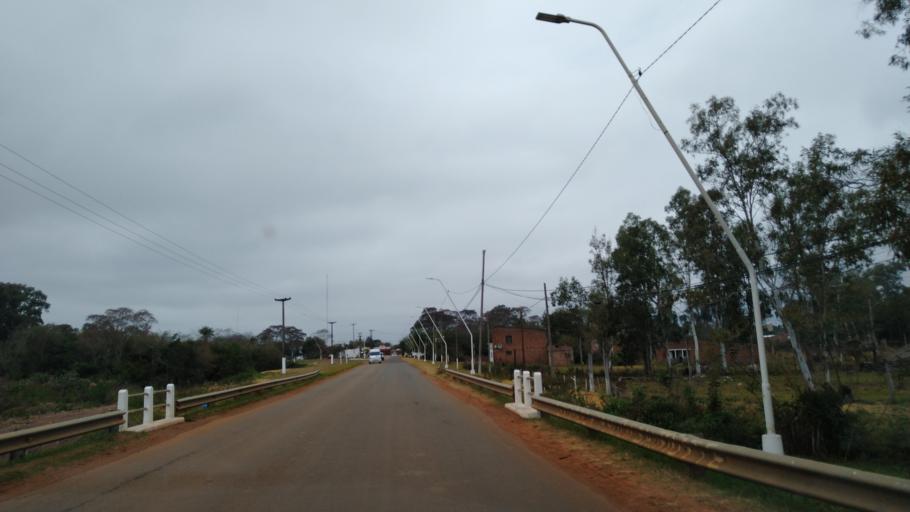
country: AR
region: Corrientes
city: Alvear
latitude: -29.0869
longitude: -56.5510
